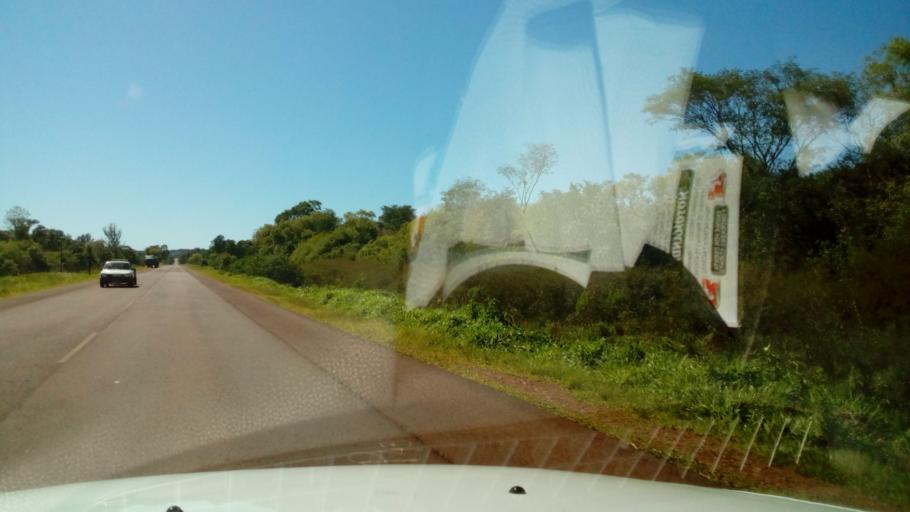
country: AR
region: Misiones
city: Almafuerte
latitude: -27.5697
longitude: -55.3948
